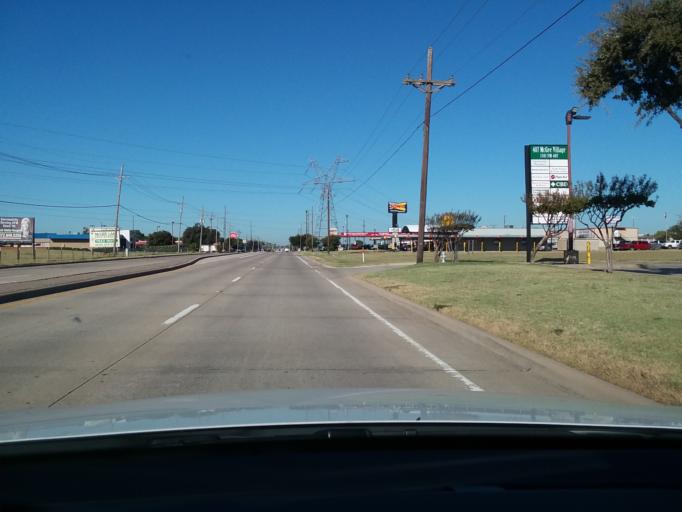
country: US
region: Texas
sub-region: Denton County
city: Highland Village
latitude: 33.0715
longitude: -97.0299
